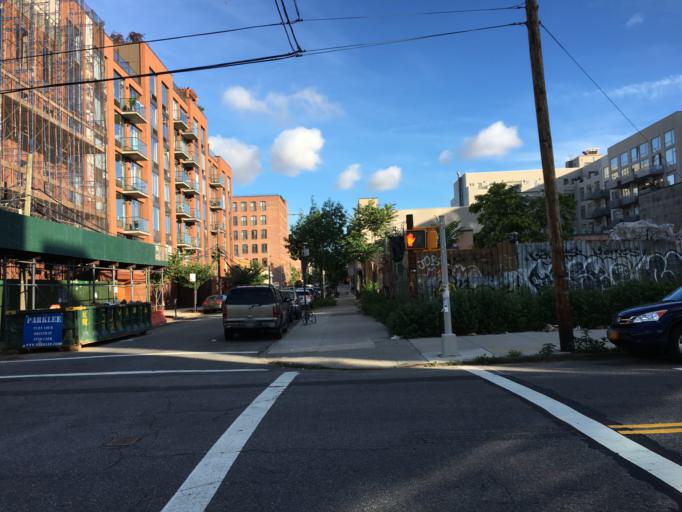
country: US
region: New York
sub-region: Queens County
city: Long Island City
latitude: 40.7179
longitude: -73.9533
